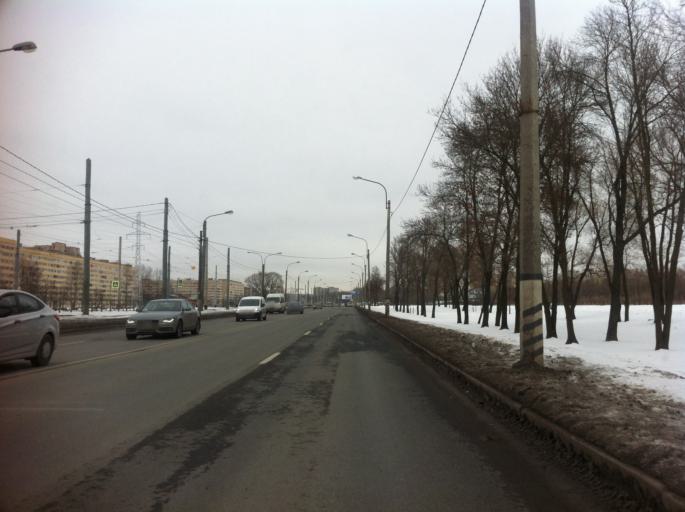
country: RU
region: St.-Petersburg
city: Uritsk
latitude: 59.8459
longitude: 30.1962
